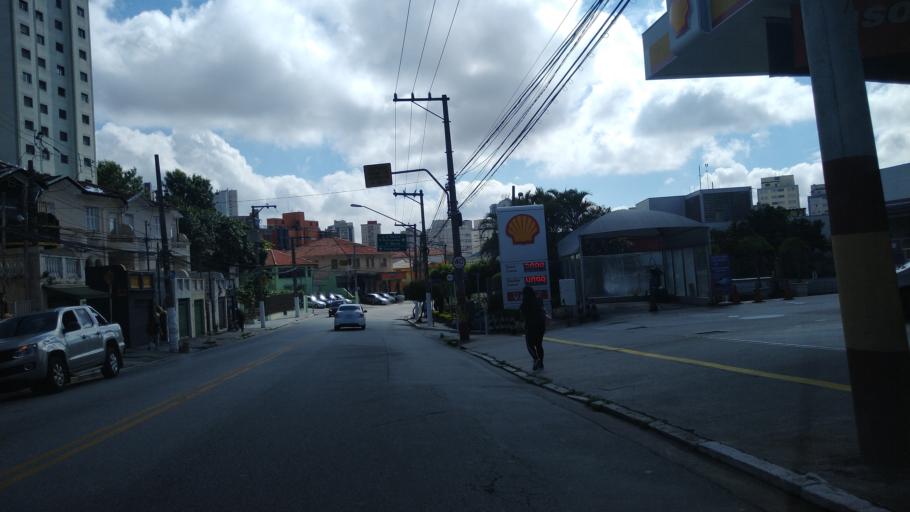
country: BR
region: Sao Paulo
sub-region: Sao Paulo
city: Sao Paulo
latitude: -23.4870
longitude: -46.6205
